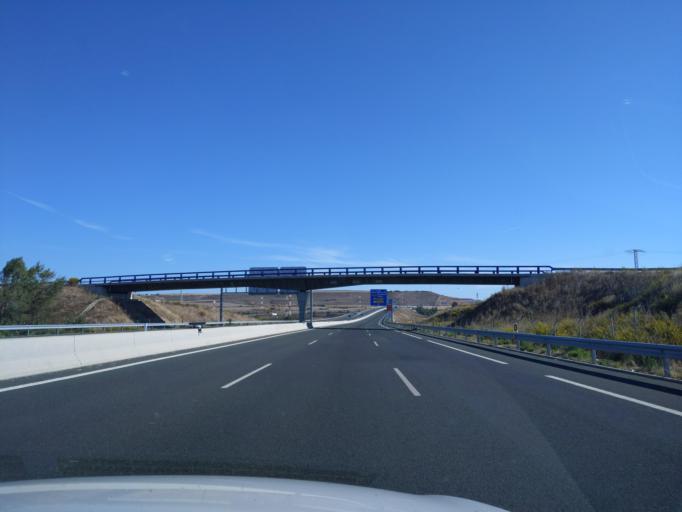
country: ES
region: Navarre
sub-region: Provincia de Navarra
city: Viana
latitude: 42.4692
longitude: -2.3630
